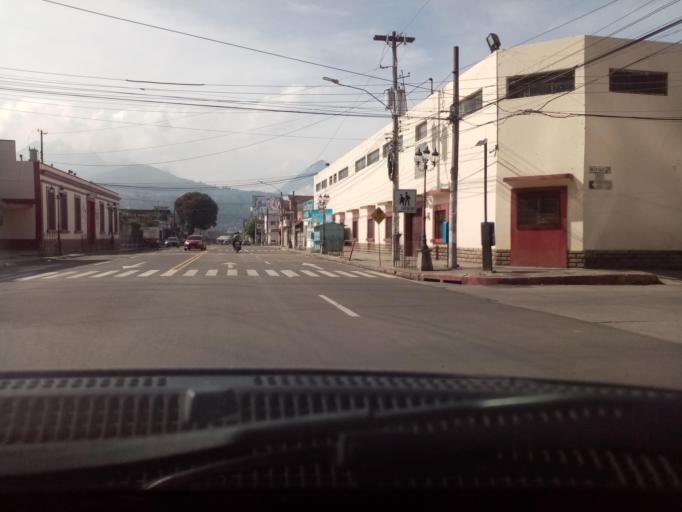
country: GT
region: Quetzaltenango
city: Quetzaltenango
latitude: 14.8429
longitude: -91.5234
